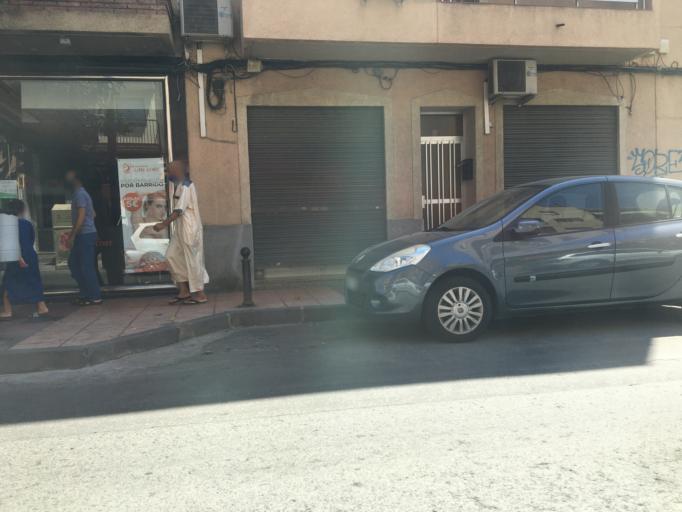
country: ES
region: Murcia
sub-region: Murcia
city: Murcia
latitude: 37.9935
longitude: -1.1022
